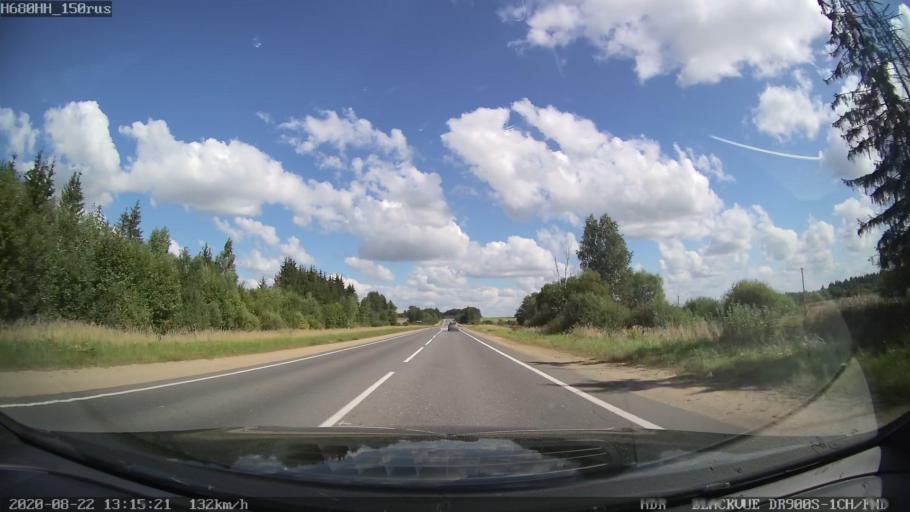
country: RU
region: Tverskaya
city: Bezhetsk
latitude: 57.7573
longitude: 36.6253
